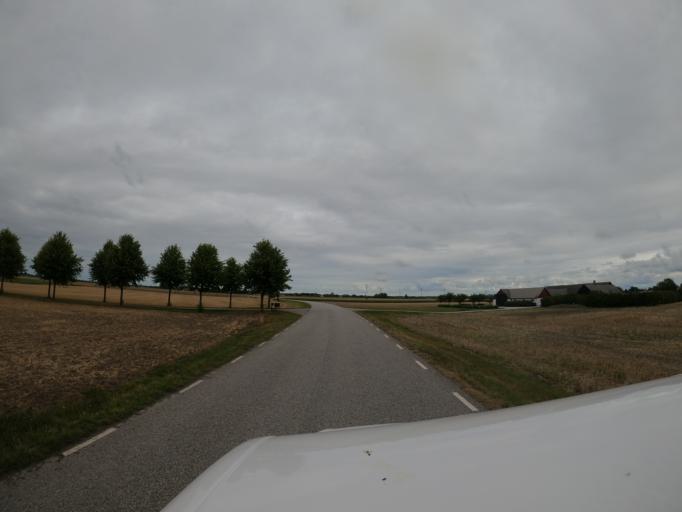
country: SE
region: Skane
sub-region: Lunds Kommun
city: Lund
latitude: 55.7541
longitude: 13.1721
